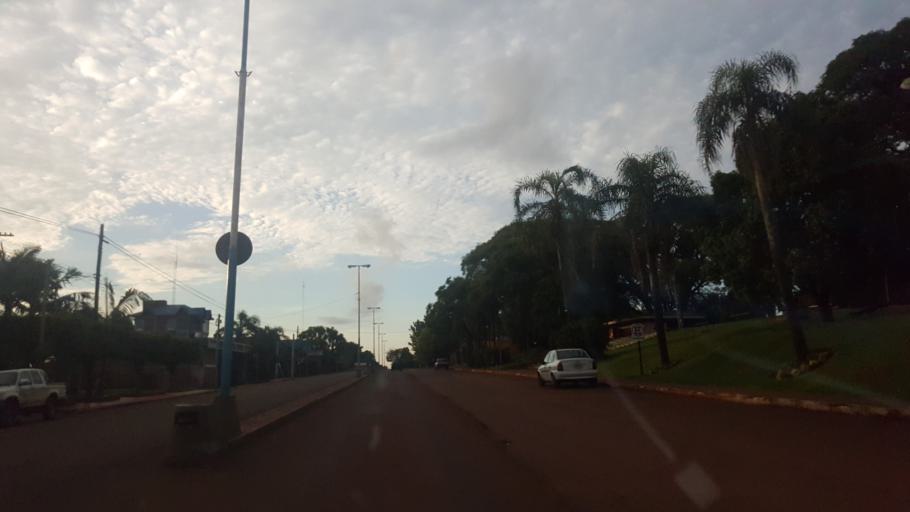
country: AR
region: Misiones
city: Dos de Mayo
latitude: -27.0216
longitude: -54.6869
